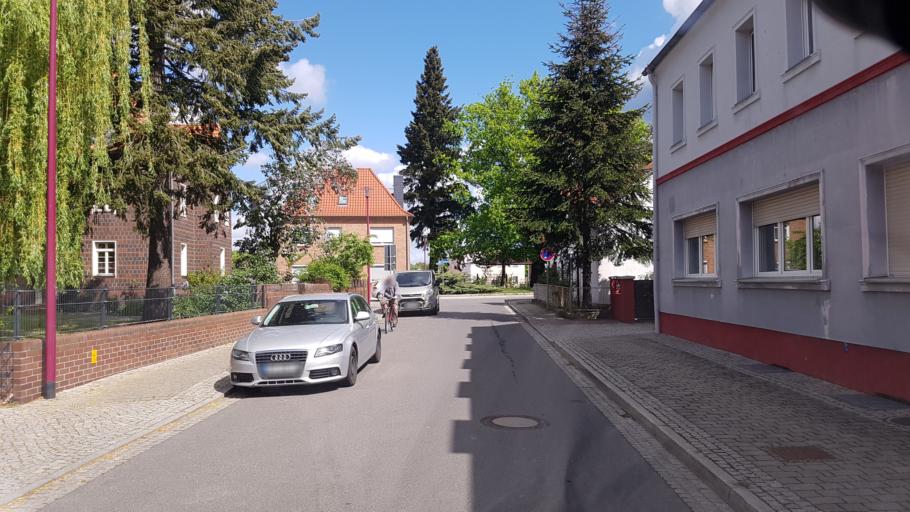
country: DE
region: Brandenburg
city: Grossraschen
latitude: 51.5883
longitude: 14.0135
